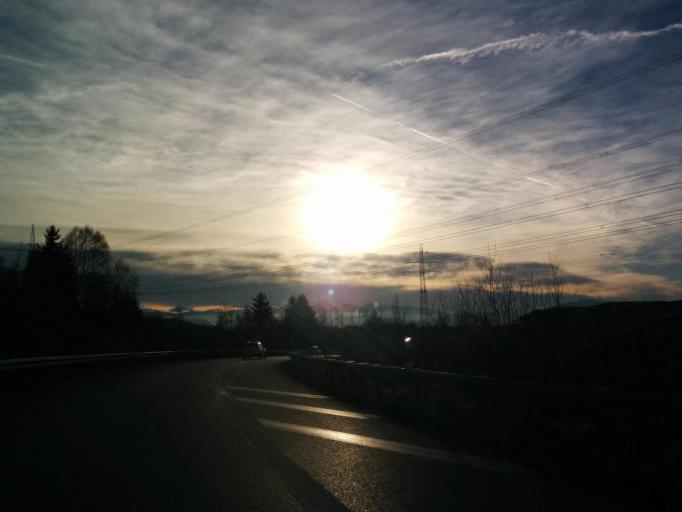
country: DE
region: Bavaria
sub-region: Swabia
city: Durach
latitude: 47.6893
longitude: 10.3666
